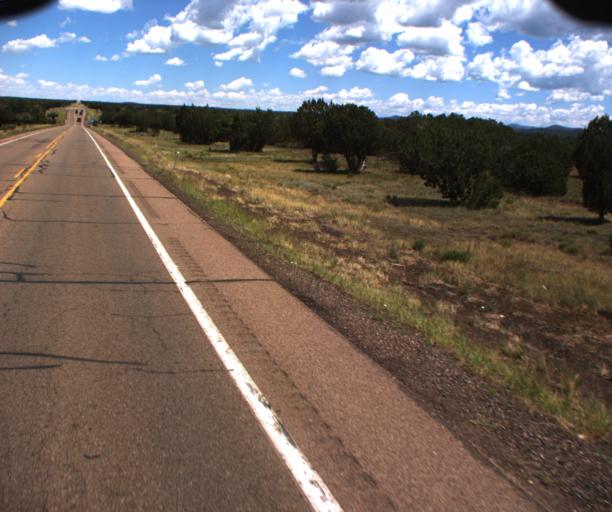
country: US
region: Arizona
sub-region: Navajo County
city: Show Low
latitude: 34.2677
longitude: -109.9412
